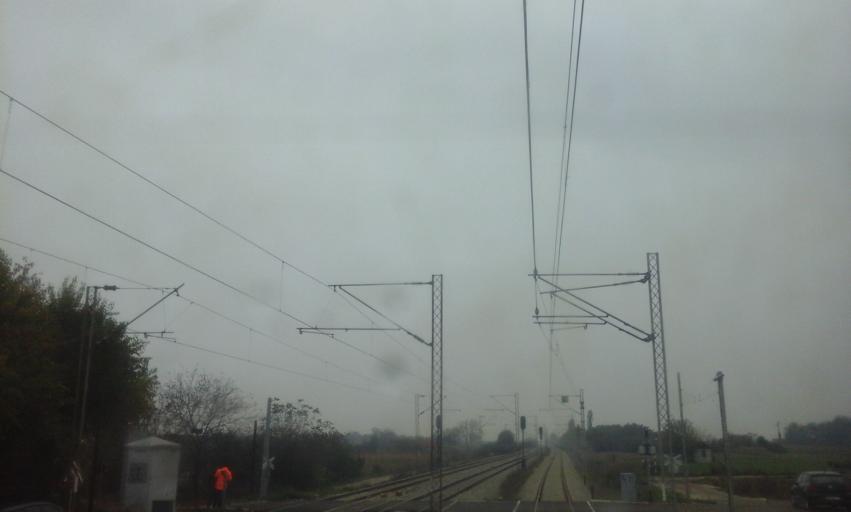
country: RS
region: Central Serbia
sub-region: Pomoravski Okrug
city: Paracin
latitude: 43.8741
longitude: 21.3921
